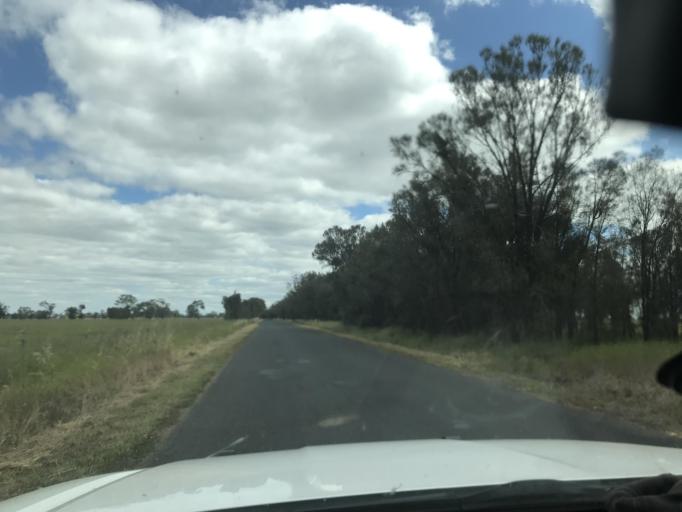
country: AU
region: South Australia
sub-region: Naracoorte and Lucindale
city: Naracoorte
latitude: -36.9006
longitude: 141.1111
